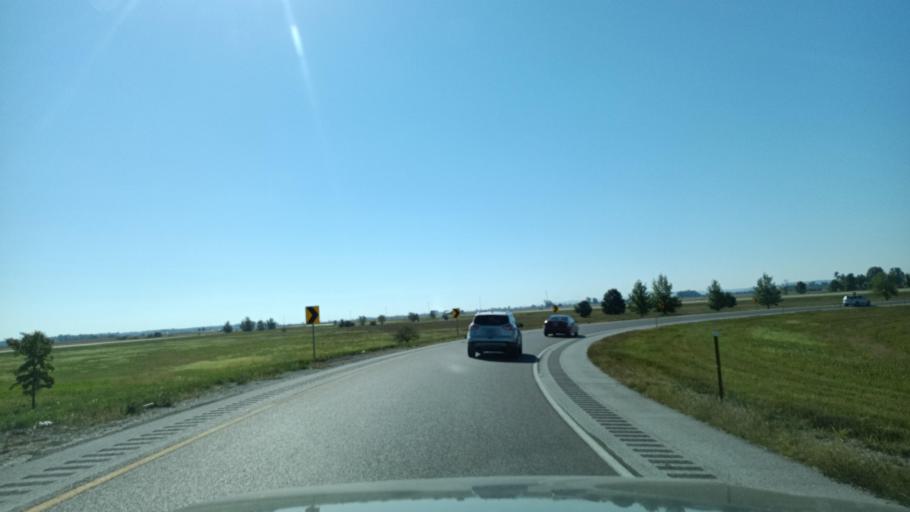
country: US
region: Missouri
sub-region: Marion County
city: Hannibal
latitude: 39.7548
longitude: -91.3188
